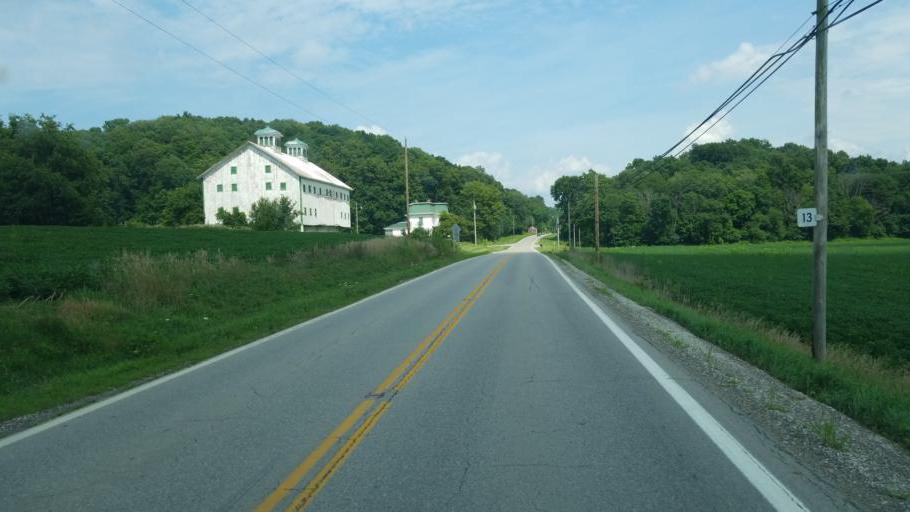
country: US
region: Ohio
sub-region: Sandusky County
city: Bellville
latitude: 40.6055
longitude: -82.4566
